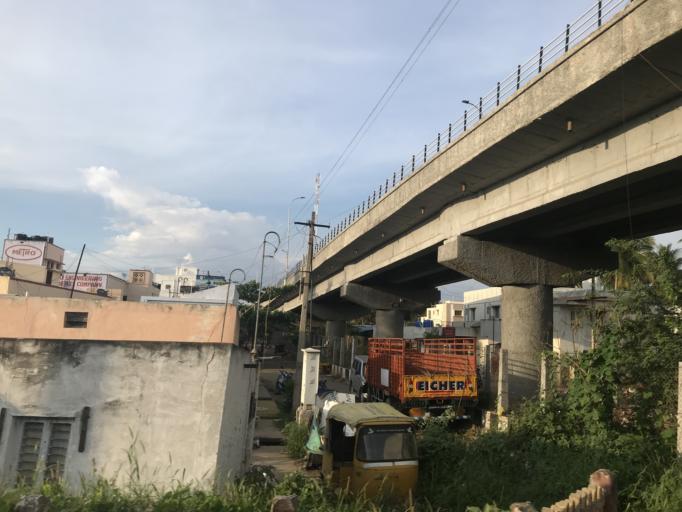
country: IN
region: Tamil Nadu
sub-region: Coimbatore
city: Coimbatore
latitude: 11.0314
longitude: 76.9657
